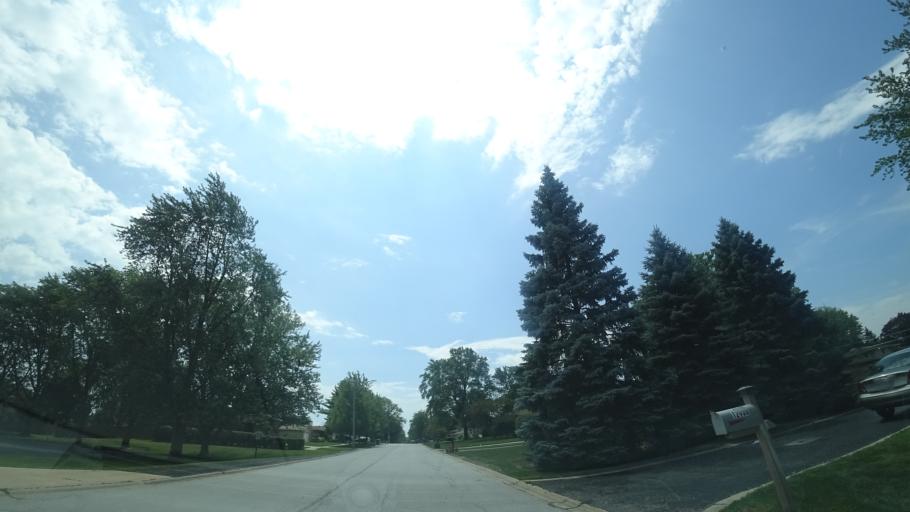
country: US
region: Illinois
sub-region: Cook County
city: Crestwood
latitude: 41.6651
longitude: -87.7682
